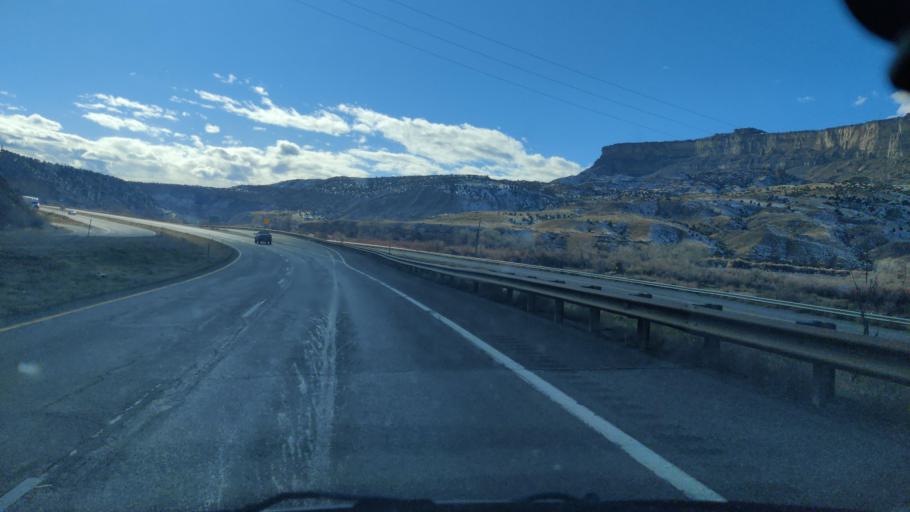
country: US
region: Colorado
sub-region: Mesa County
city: Palisade
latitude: 39.1475
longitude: -108.3144
